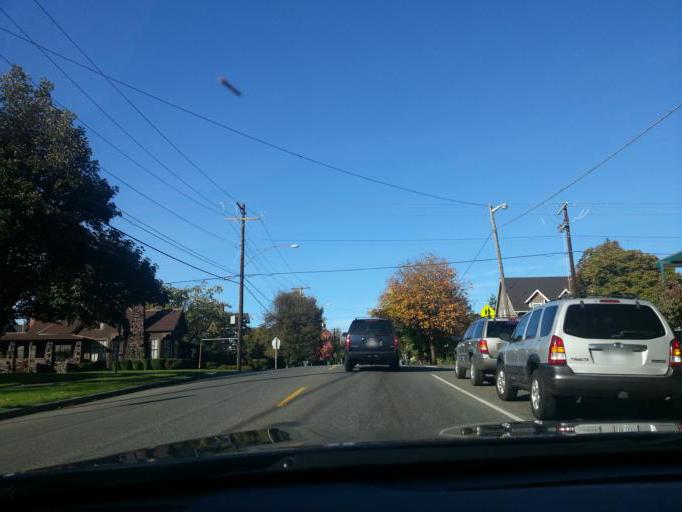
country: US
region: Washington
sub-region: Snohomish County
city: Snohomish
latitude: 47.9141
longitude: -122.0984
